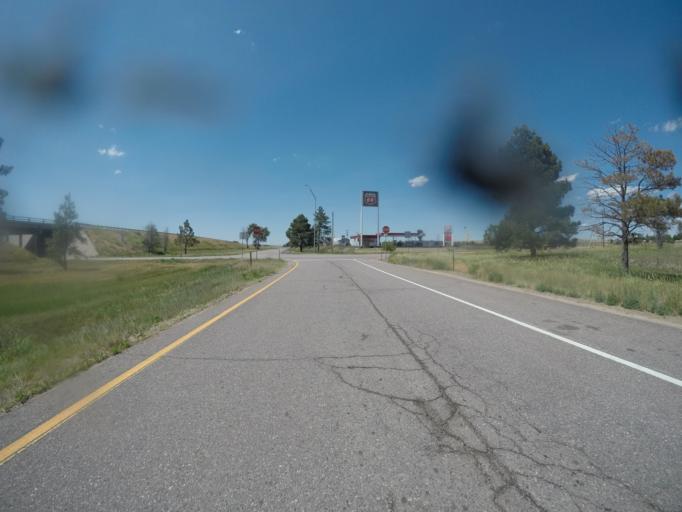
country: US
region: Colorado
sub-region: Arapahoe County
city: Byers
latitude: 39.6145
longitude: -104.0395
